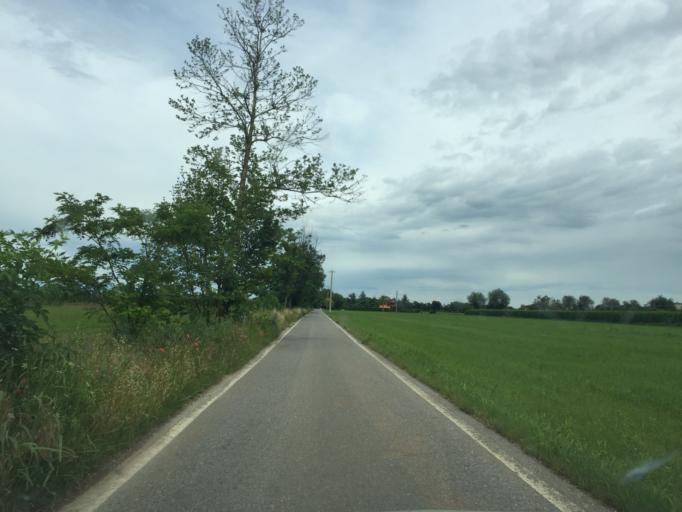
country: IT
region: Lombardy
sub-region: Provincia di Brescia
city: Castenedolo
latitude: 45.4509
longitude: 10.2703
